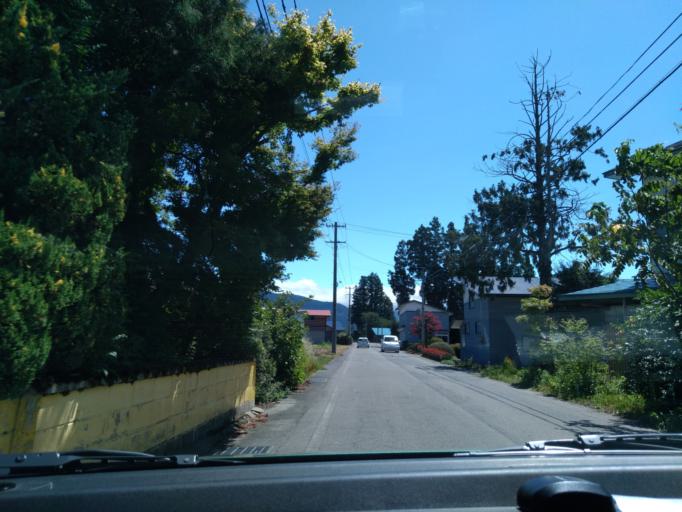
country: JP
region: Akita
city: Kakunodatemachi
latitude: 39.5292
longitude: 140.6032
